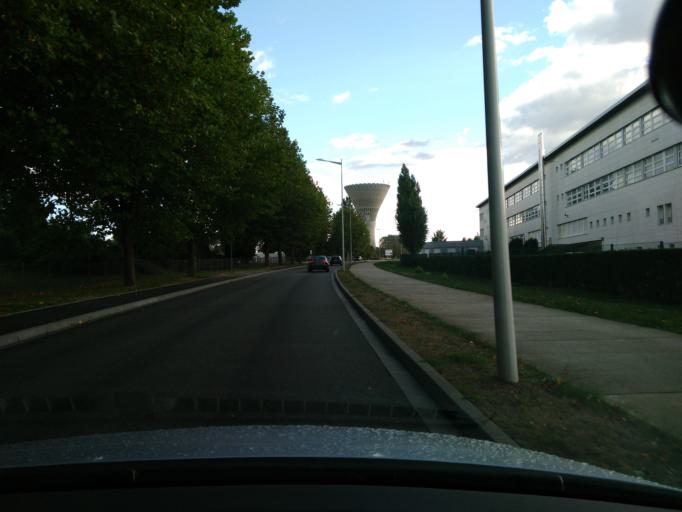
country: FR
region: Haute-Normandie
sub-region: Departement de l'Eure
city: Evreux
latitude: 49.0192
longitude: 1.1715
